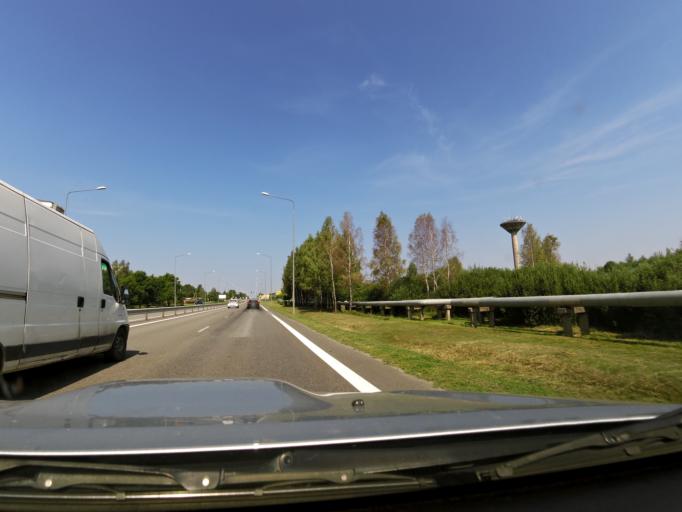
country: LT
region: Siauliu apskritis
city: Radviliskis
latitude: 55.8213
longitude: 23.5325
